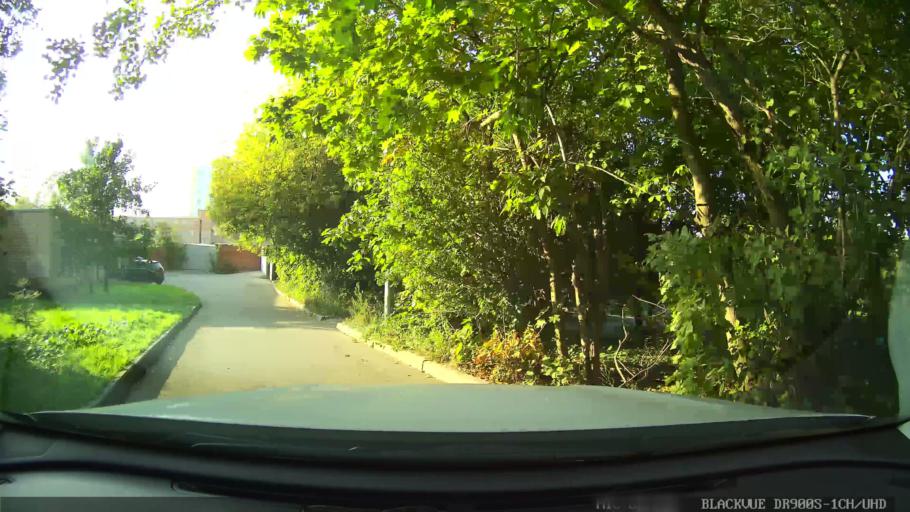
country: RU
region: Moscow
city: Nikol'skoye
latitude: 55.6824
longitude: 37.4958
